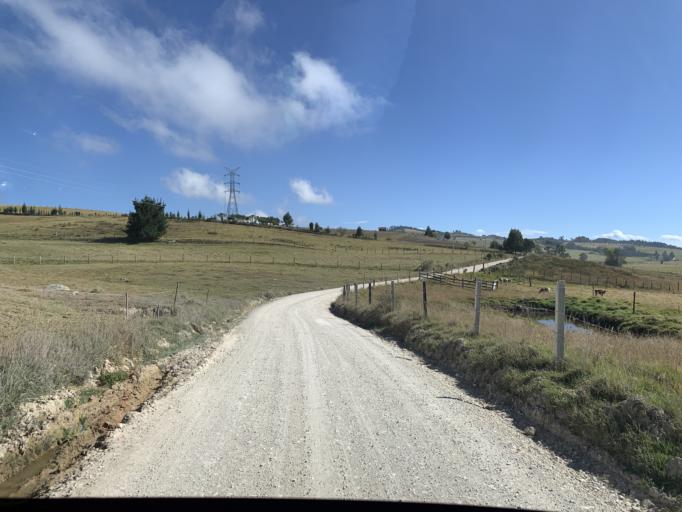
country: CO
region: Boyaca
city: Tuta
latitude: 5.6732
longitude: -73.1483
